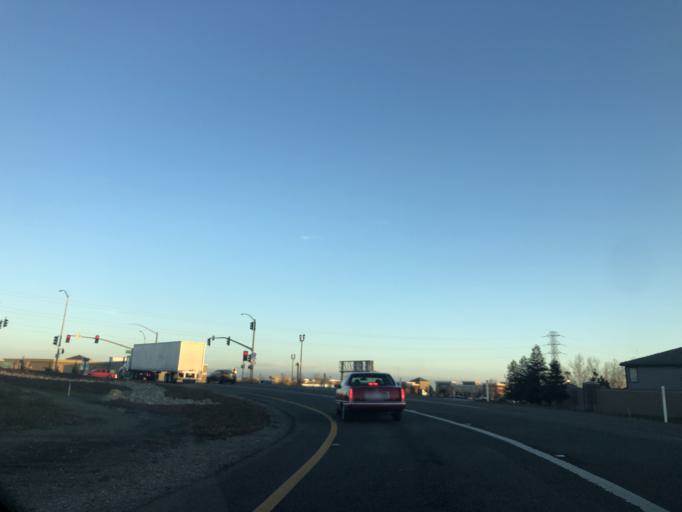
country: US
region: California
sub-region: Yolo County
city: Woodland
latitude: 38.6727
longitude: -121.7297
